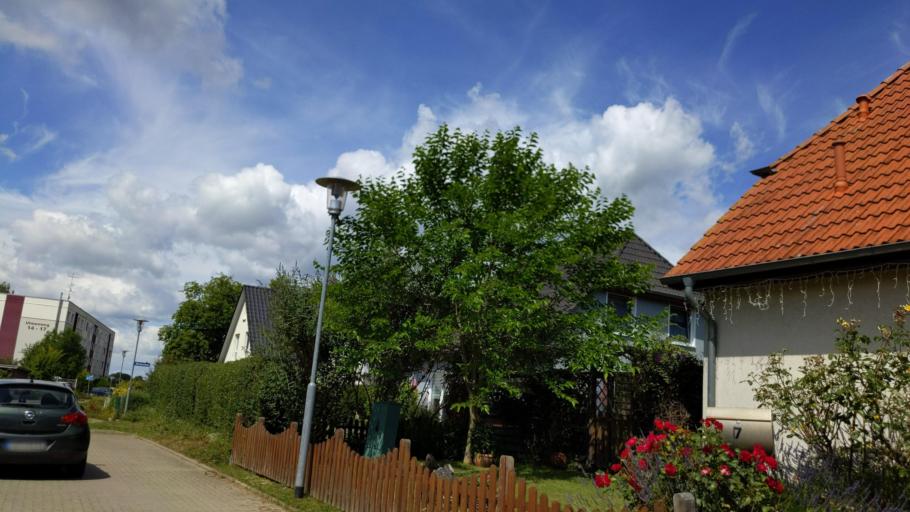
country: DE
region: Mecklenburg-Vorpommern
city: Dassow
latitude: 53.9032
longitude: 10.9771
